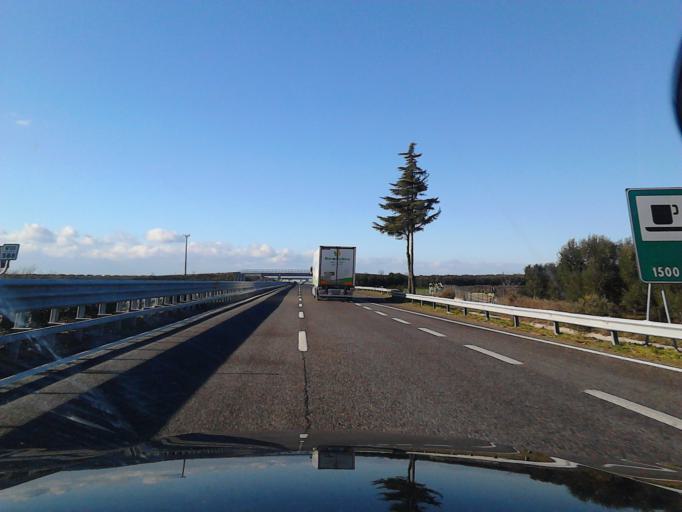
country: IT
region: Apulia
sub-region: Provincia di Foggia
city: Cerignola
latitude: 41.3248
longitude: 15.8934
